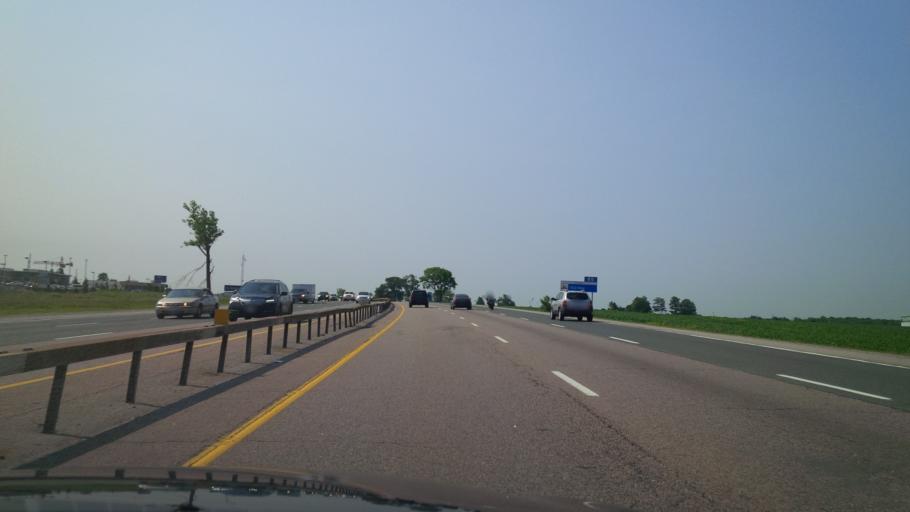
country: CA
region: Ontario
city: Innisfil
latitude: 44.3026
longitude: -79.6840
